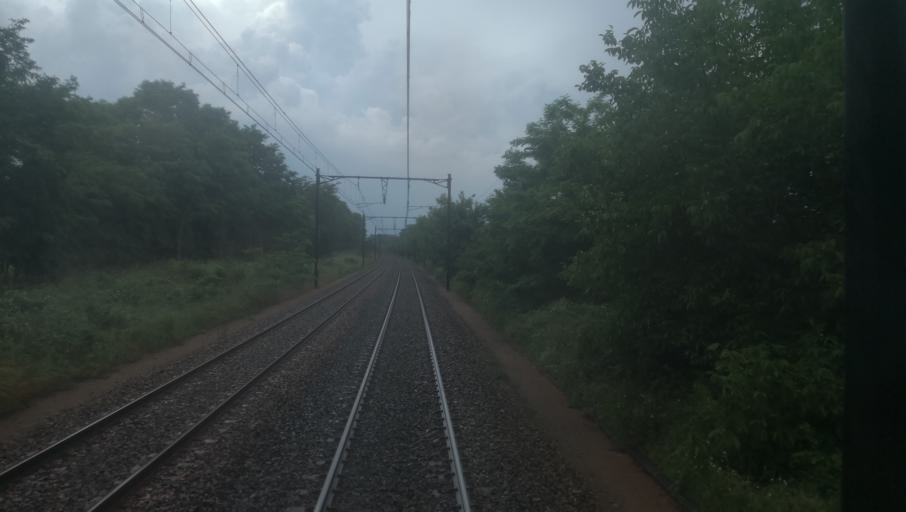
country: FR
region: Centre
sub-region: Departement du Loiret
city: Saint-Cyr-en-Val
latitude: 47.8321
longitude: 1.9488
